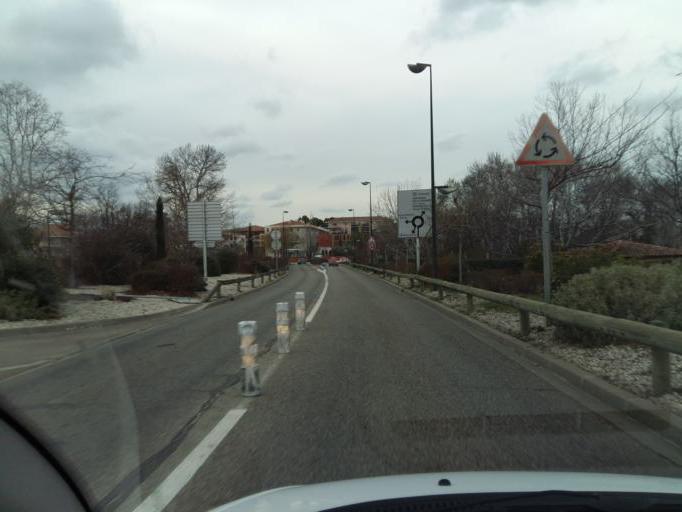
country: FR
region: Provence-Alpes-Cote d'Azur
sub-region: Departement des Bouches-du-Rhone
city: Cabries
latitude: 43.4908
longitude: 5.3561
